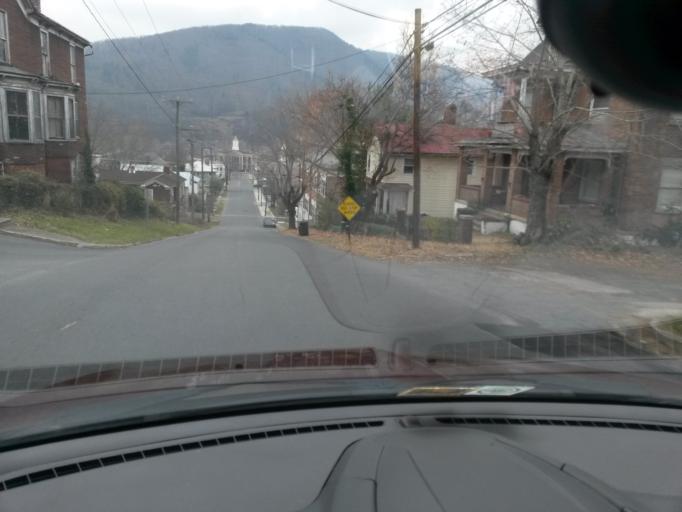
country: US
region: Virginia
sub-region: Alleghany County
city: Clifton Forge
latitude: 37.8188
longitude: -79.8230
